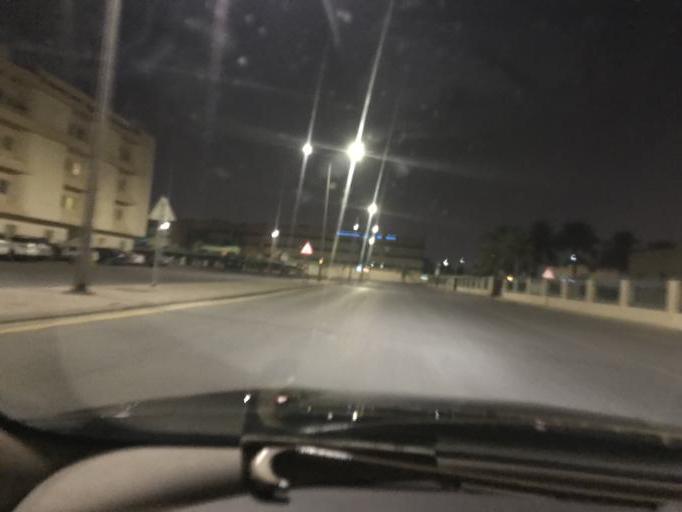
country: SA
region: Ar Riyad
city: Riyadh
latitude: 24.7978
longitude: 46.7091
